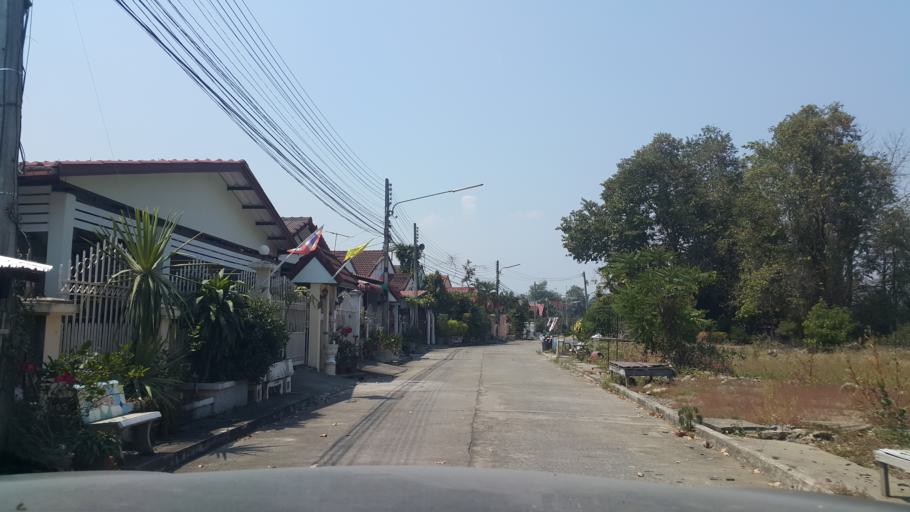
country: TH
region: Chiang Mai
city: San Kamphaeng
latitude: 18.7729
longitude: 99.0731
